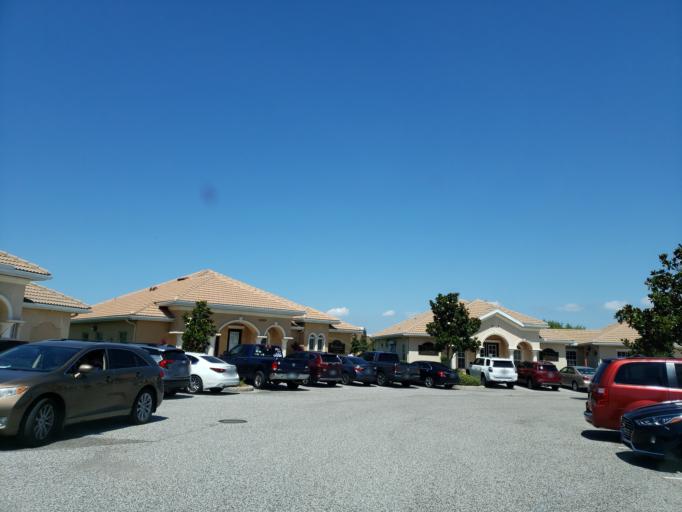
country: US
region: Florida
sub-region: Hillsborough County
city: Brandon
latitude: 27.9189
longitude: -82.3245
